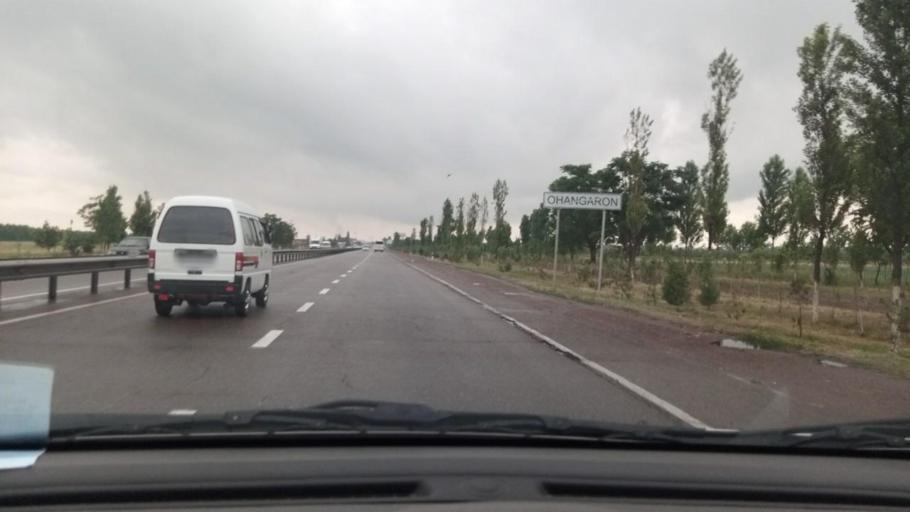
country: UZ
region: Toshkent
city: Ohangaron
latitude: 40.9153
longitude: 69.6074
